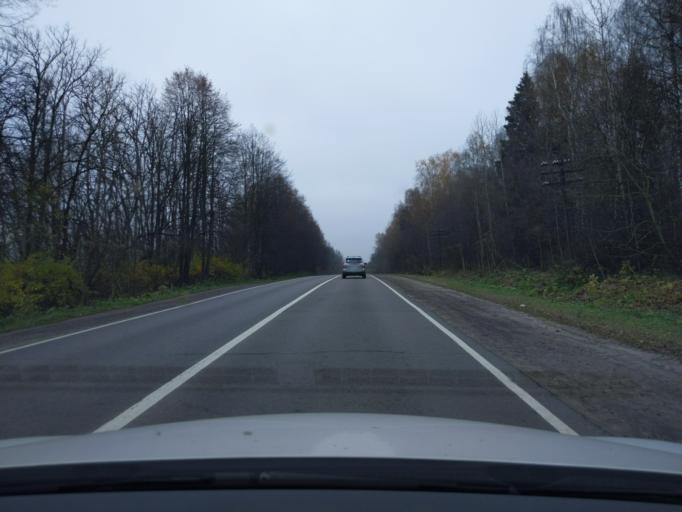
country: RU
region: Moskovskaya
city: Ashukino
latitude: 56.1460
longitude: 37.9881
